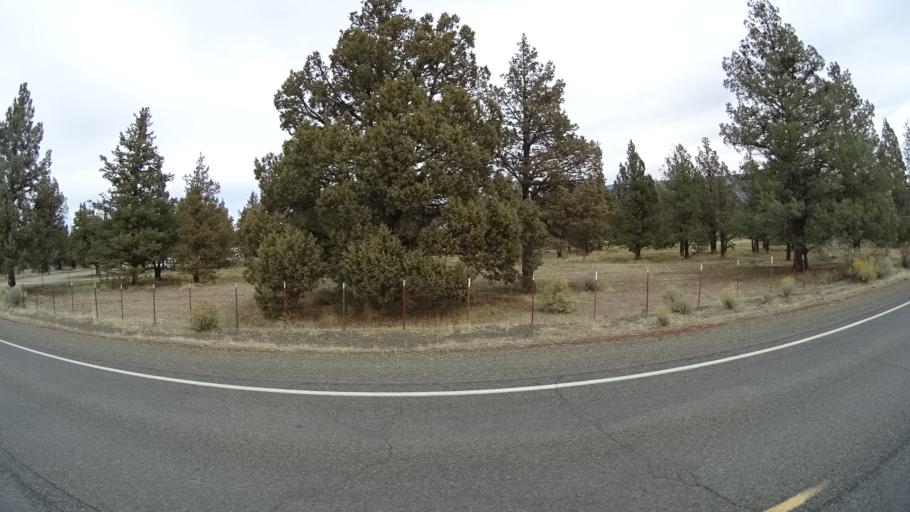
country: US
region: California
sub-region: Siskiyou County
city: Weed
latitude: 41.5998
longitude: -122.3469
